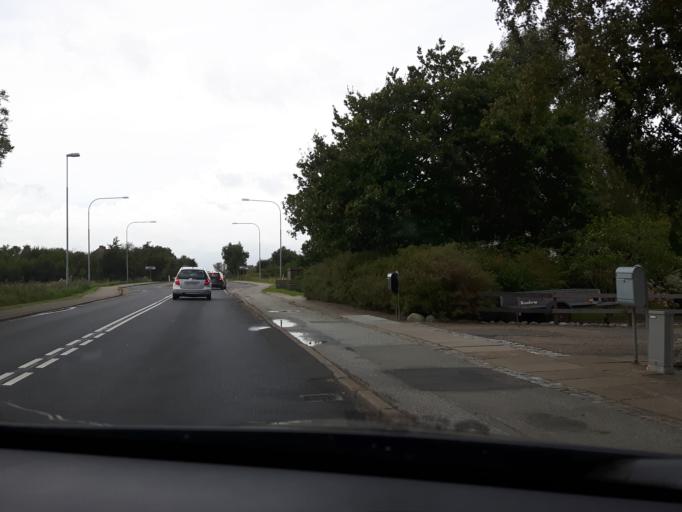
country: DK
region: North Denmark
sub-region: Jammerbugt Kommune
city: Brovst
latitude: 57.1072
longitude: 9.5733
